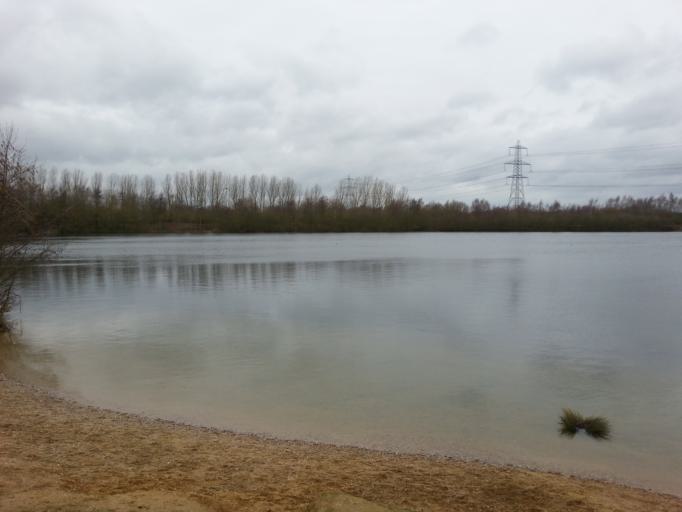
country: GB
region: England
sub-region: Lincolnshire
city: Skellingthorpe
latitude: 53.1846
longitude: -0.6443
